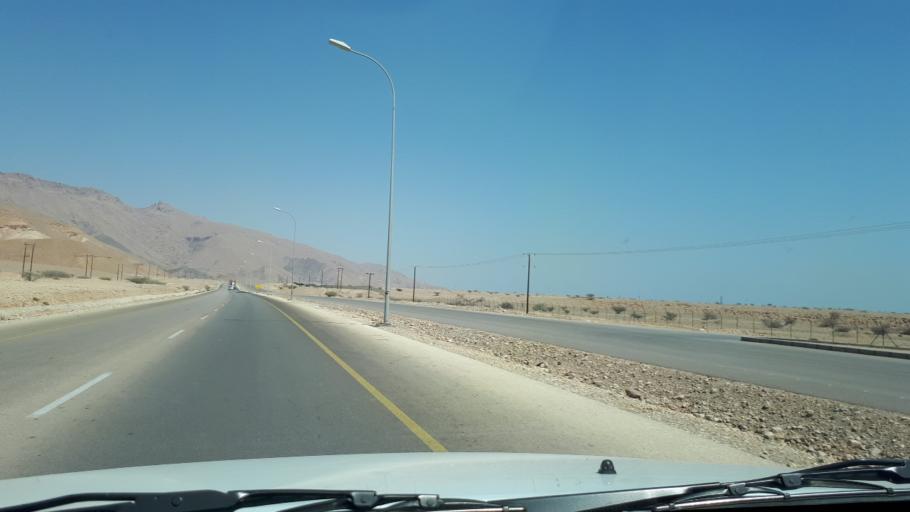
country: OM
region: Ash Sharqiyah
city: Sur
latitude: 22.6204
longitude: 59.4193
